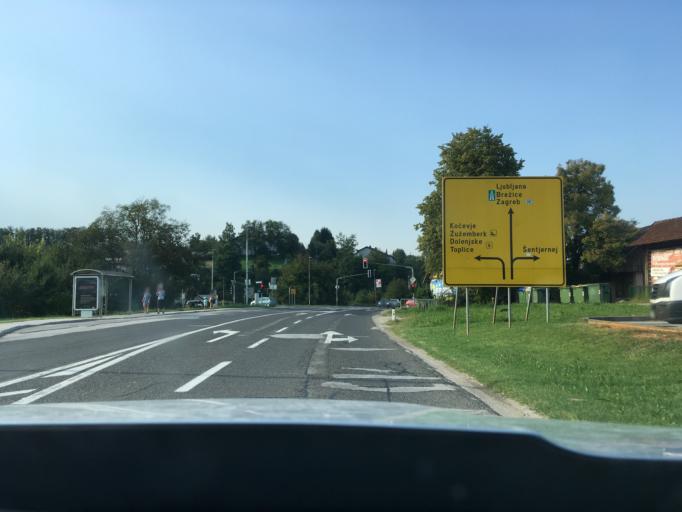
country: SI
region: Novo Mesto
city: Novo Mesto
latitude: 45.7988
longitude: 15.1802
